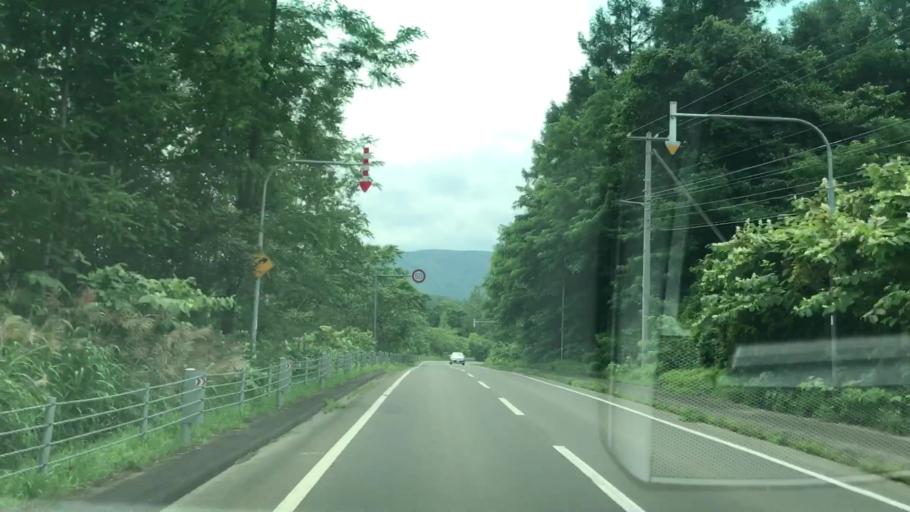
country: JP
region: Hokkaido
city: Yoichi
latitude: 43.0665
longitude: 140.8202
